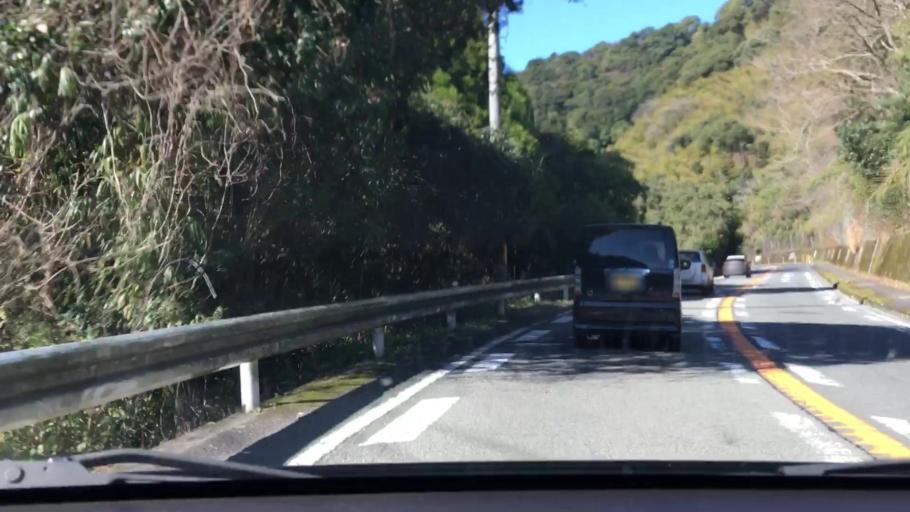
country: JP
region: Kagoshima
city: Kagoshima-shi
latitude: 31.6521
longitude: 130.5079
